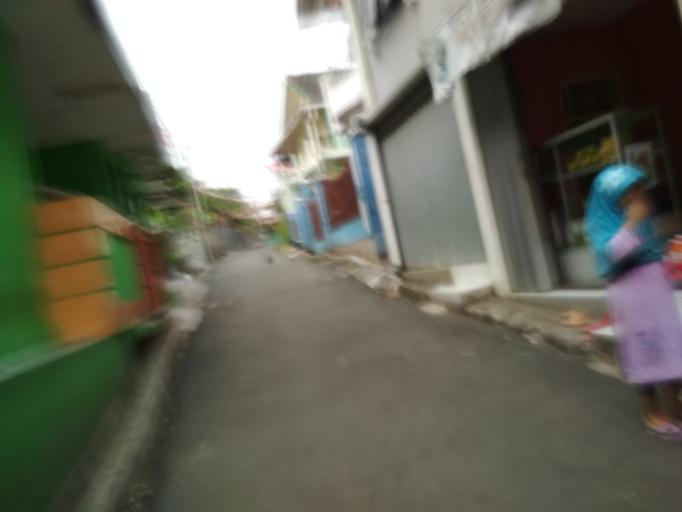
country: ID
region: West Java
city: Ciampea
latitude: -6.5569
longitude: 106.7355
